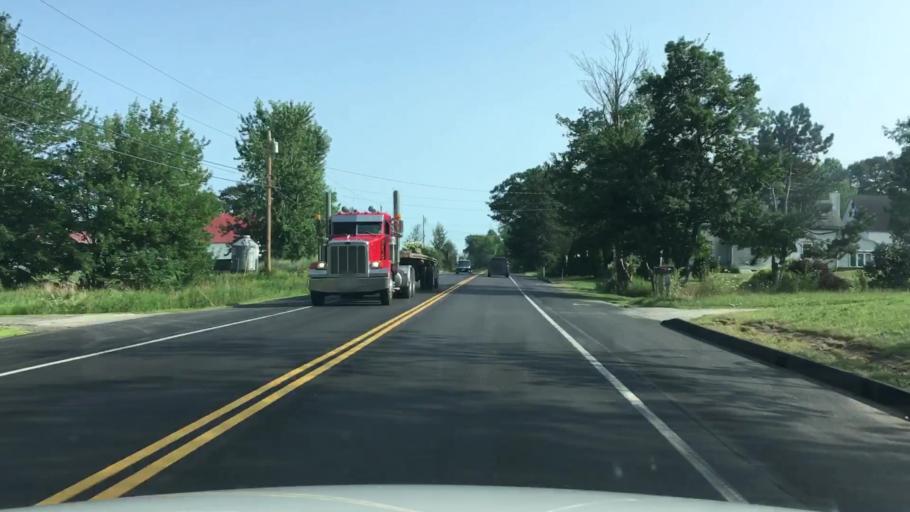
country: US
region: Maine
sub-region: Knox County
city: Warren
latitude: 44.1088
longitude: -69.2531
